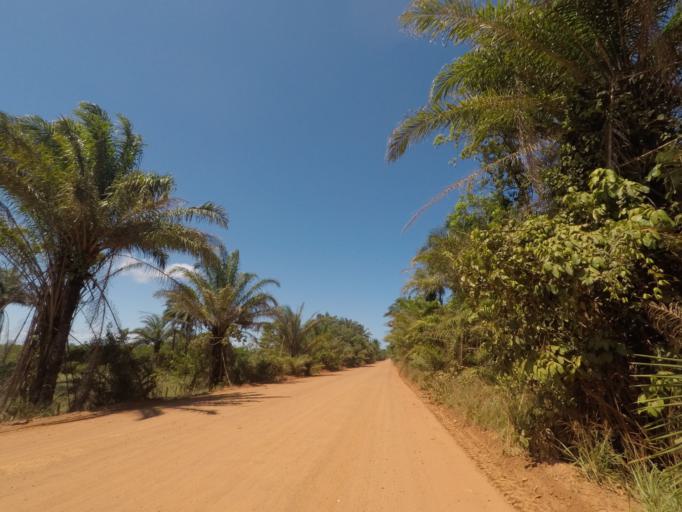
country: BR
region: Bahia
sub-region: Marau
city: Marau
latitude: -13.9637
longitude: -38.9471
